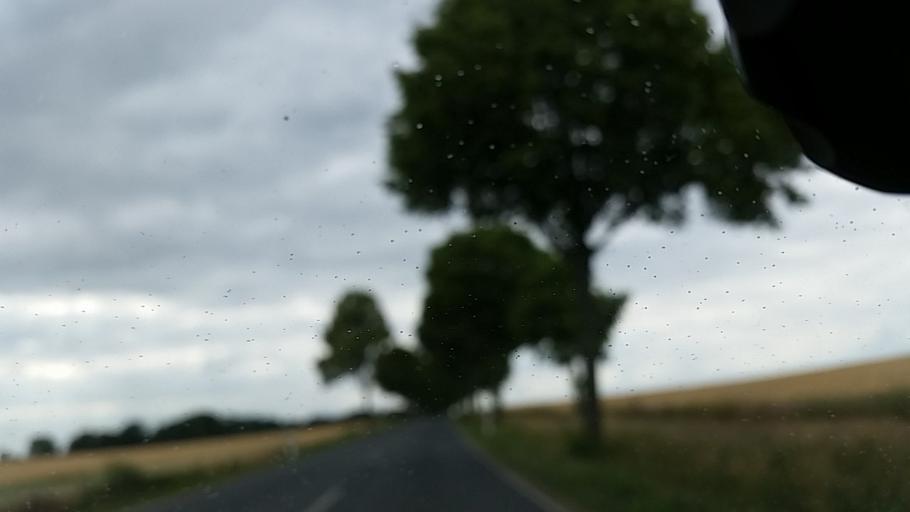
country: DE
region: Lower Saxony
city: Wolfsburg
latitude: 52.3412
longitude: 10.8145
